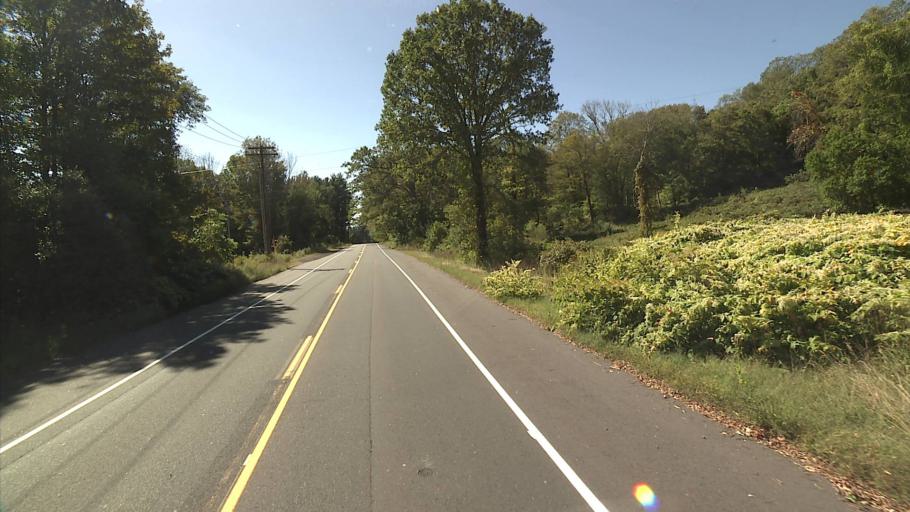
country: US
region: Connecticut
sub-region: New Haven County
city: Woodbridge
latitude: 41.3816
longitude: -72.9751
